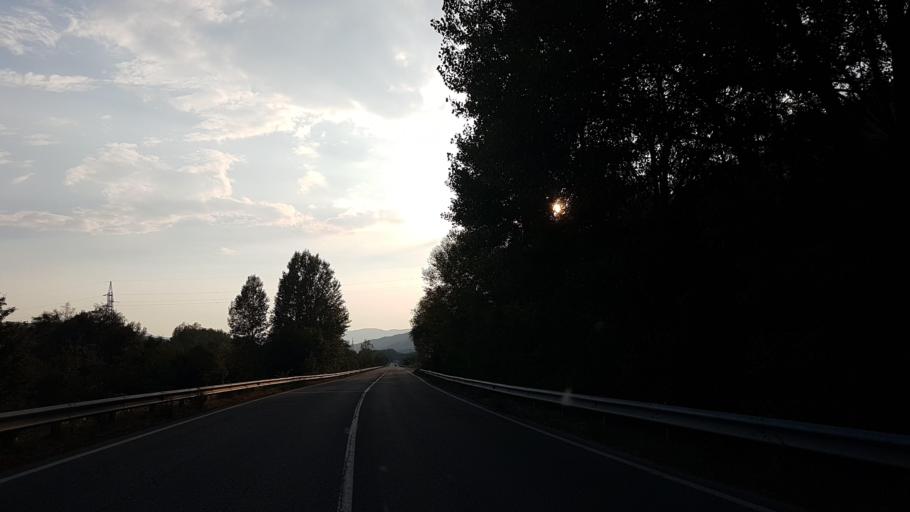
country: IT
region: Emilia-Romagna
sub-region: Provincia di Parma
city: Borgo Val di Taro
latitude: 44.4974
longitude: 9.7985
